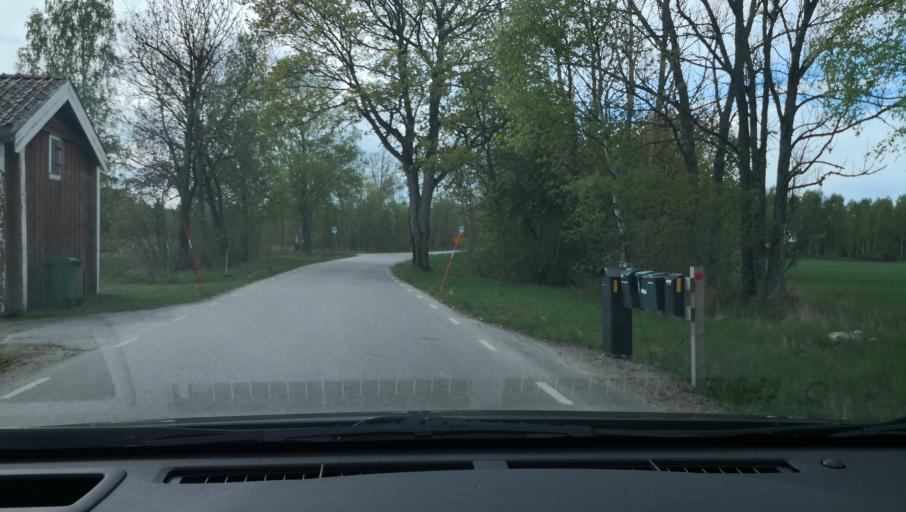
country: SE
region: OErebro
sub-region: Kumla Kommun
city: Hallabrottet
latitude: 59.1576
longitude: 15.2135
